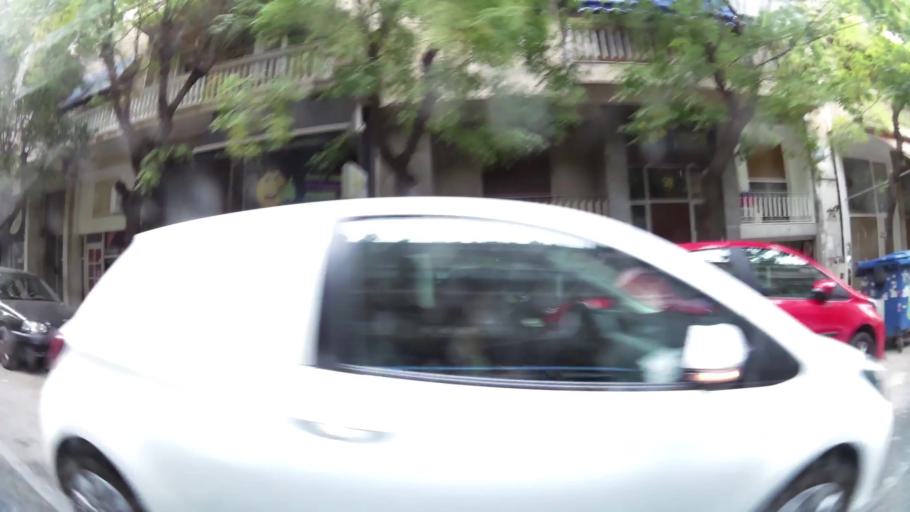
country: GR
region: Attica
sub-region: Nomarchia Athinas
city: Vyronas
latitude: 37.9701
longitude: 23.7521
